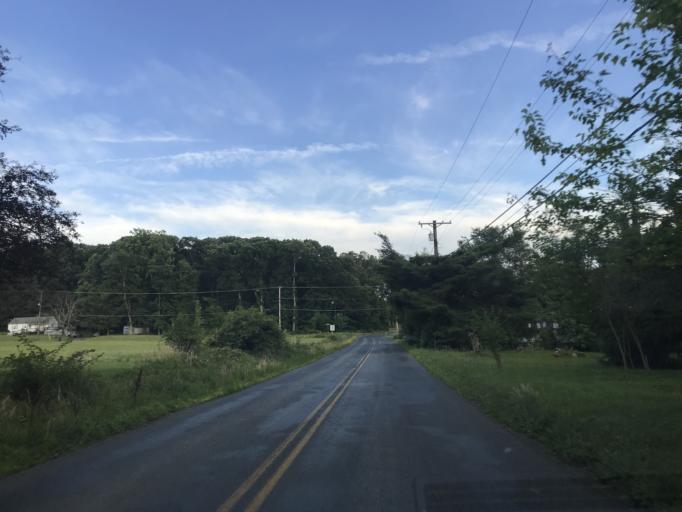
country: US
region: Maryland
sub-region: Harford County
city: Aberdeen
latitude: 39.5317
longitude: -76.2202
